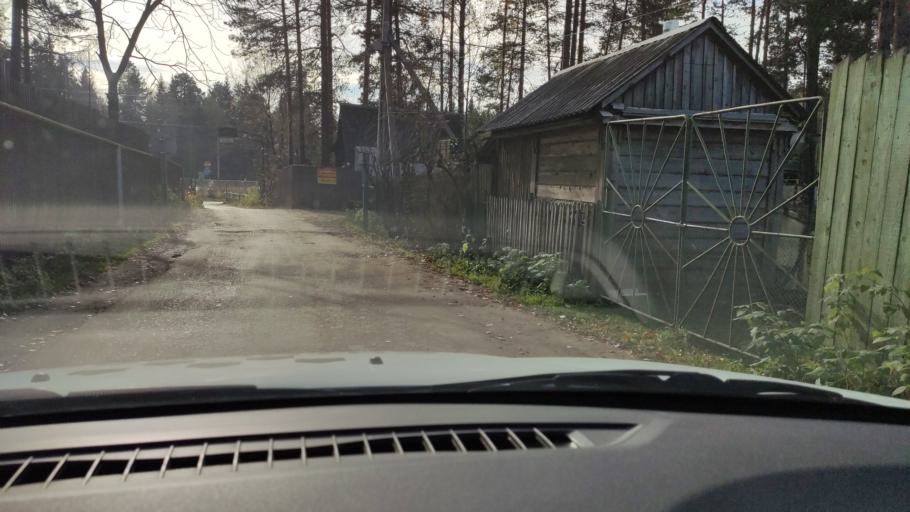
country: RU
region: Perm
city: Kondratovo
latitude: 58.0550
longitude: 56.1317
